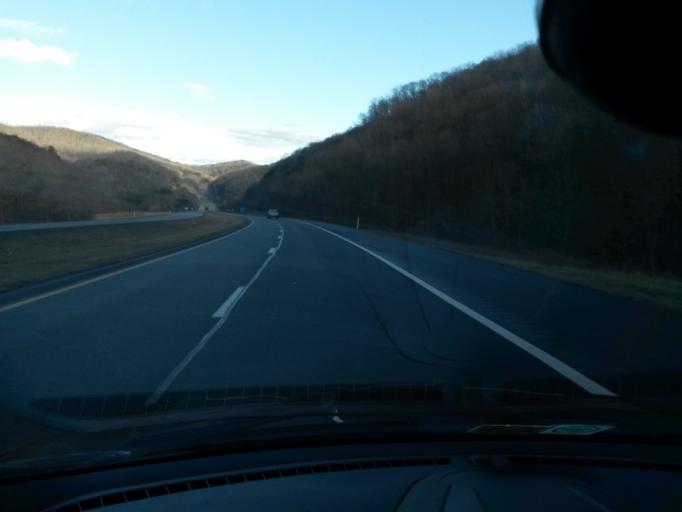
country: US
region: West Virginia
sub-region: Mercer County
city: Athens
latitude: 37.3395
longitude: -80.9690
